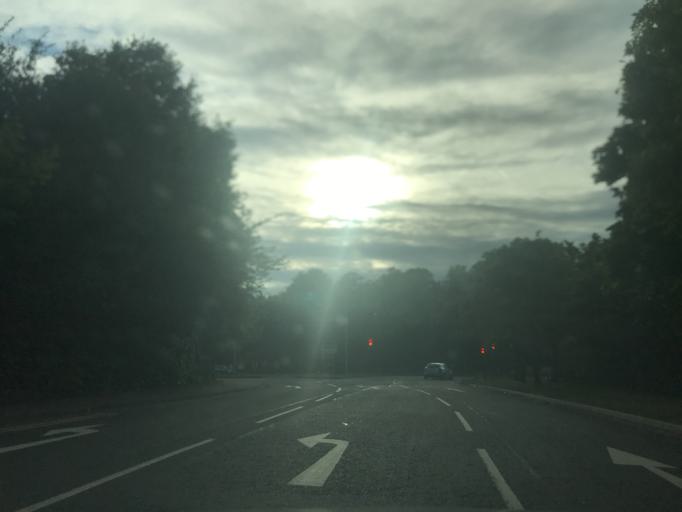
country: GB
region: England
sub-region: Bracknell Forest
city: Bracknell
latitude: 51.4126
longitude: -0.7492
